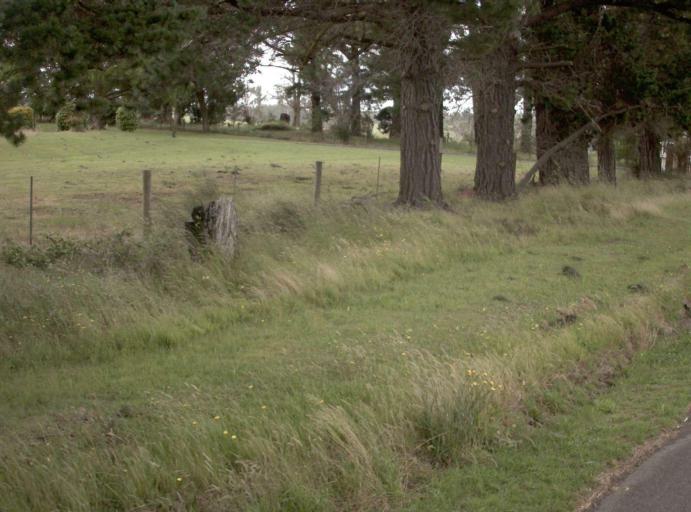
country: AU
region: Victoria
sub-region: Baw Baw
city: Warragul
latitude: -38.0938
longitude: 145.8518
